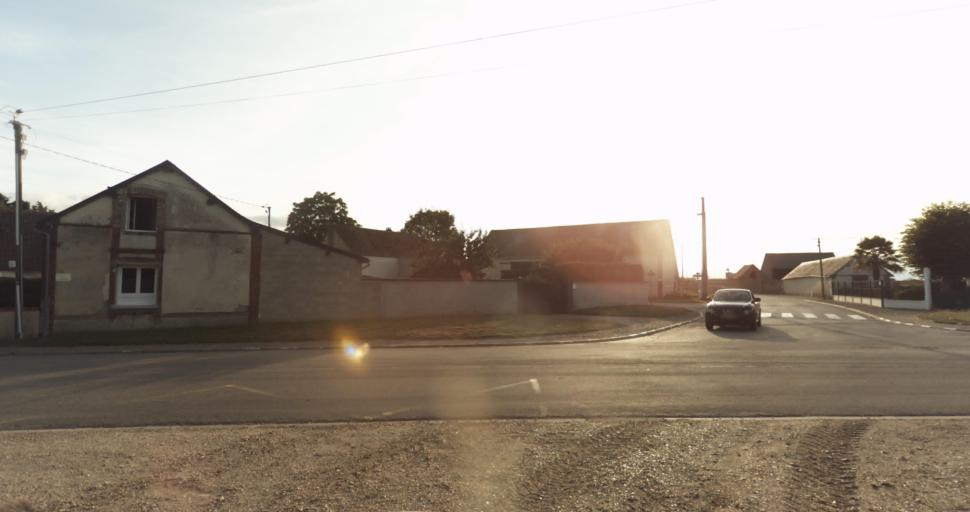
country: FR
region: Haute-Normandie
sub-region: Departement de l'Eure
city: Marcilly-sur-Eure
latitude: 48.8477
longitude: 1.2744
